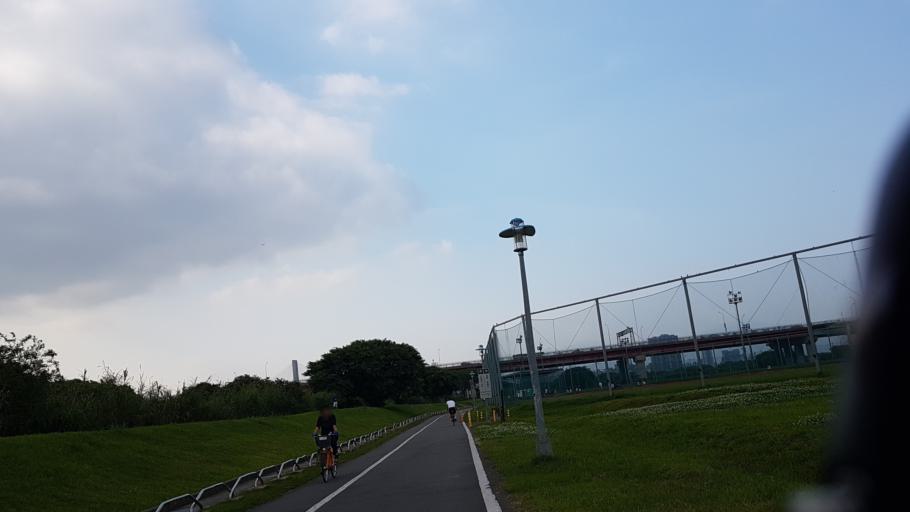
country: TW
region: Taipei
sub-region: Taipei
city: Banqiao
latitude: 25.0333
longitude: 121.4863
